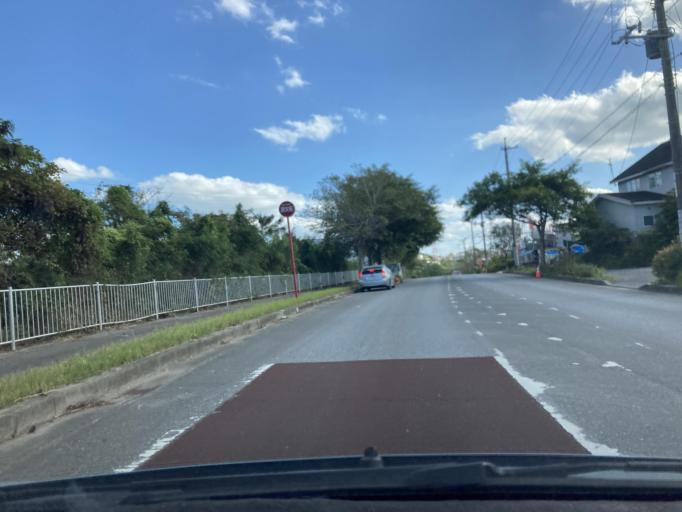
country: JP
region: Okinawa
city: Gushikawa
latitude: 26.3677
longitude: 127.8402
